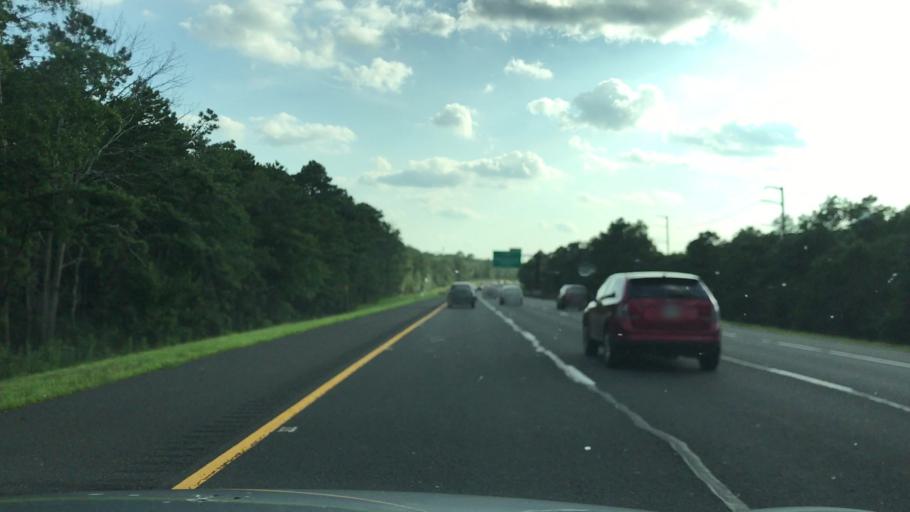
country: US
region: New Jersey
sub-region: Ocean County
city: Tuckerton
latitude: 39.6598
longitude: -74.3306
